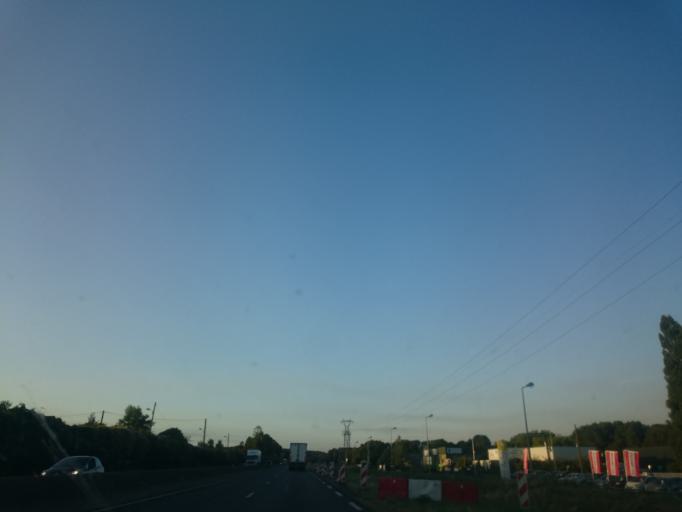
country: FR
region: Ile-de-France
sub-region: Departement de l'Essonne
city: Etrechy
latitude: 48.4899
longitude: 2.1973
